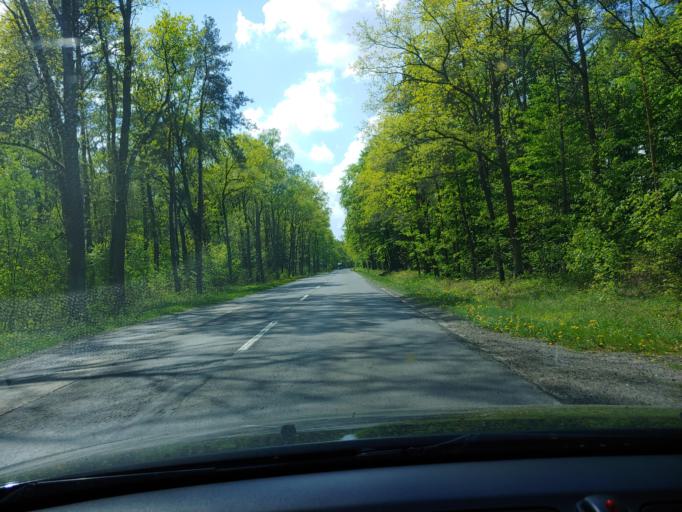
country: PL
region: Subcarpathian Voivodeship
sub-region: Powiat mielecki
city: Trzciana
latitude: 50.2626
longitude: 21.3521
